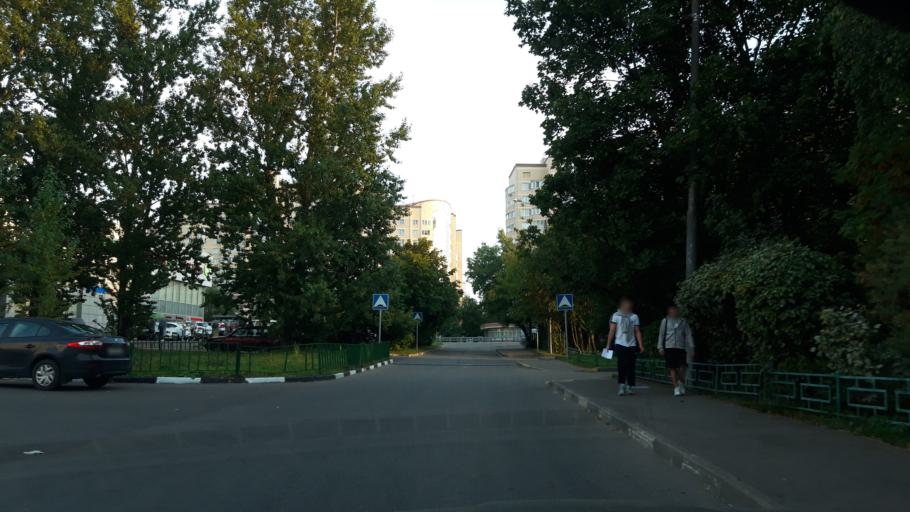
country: RU
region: Moscow
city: Zelenograd
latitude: 55.9820
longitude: 37.1835
